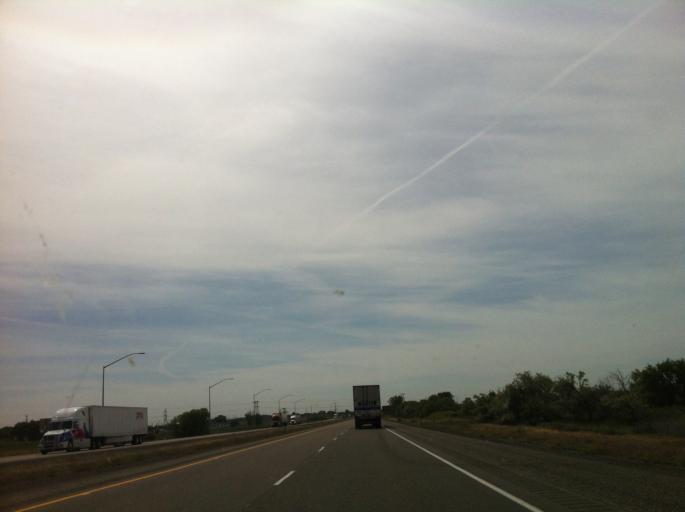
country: US
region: Oregon
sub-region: Malheur County
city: Ontario
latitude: 44.0597
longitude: -116.9907
